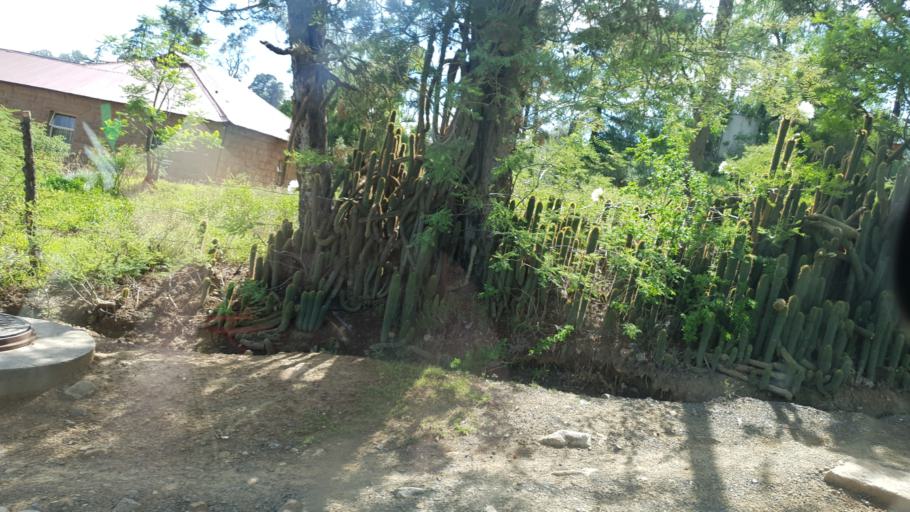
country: LS
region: Maseru
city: Nako
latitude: -29.6262
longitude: 27.5098
